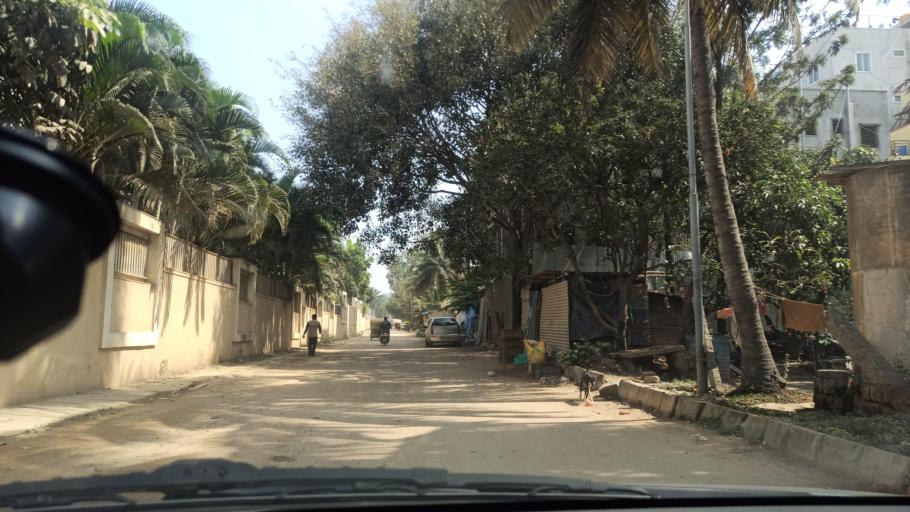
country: IN
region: Karnataka
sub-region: Bangalore Urban
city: Bangalore
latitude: 12.9356
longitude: 77.6881
